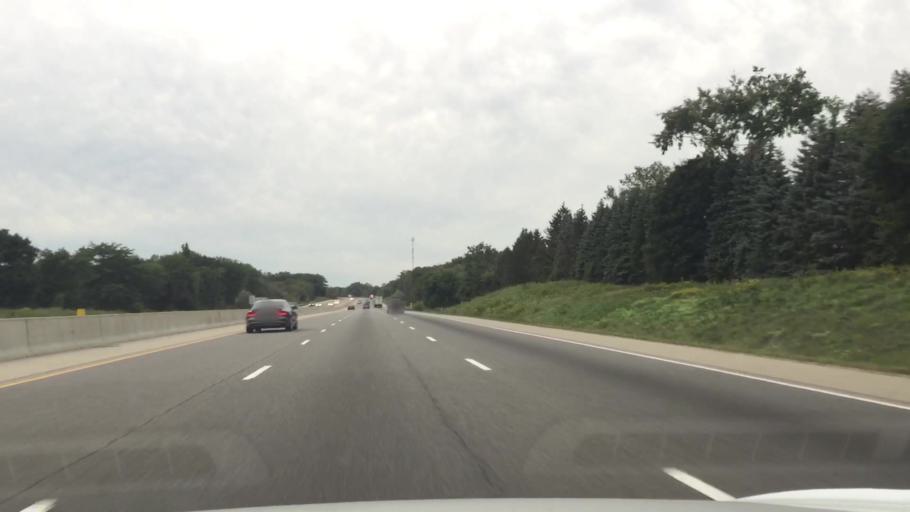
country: CA
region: Ontario
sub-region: Oxford County
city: Woodstock
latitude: 43.2090
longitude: -80.6148
